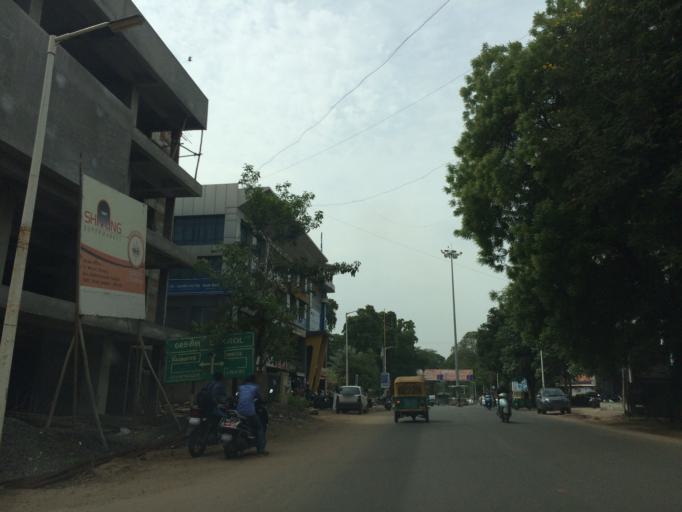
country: IN
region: Gujarat
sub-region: Anand
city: Karamsad
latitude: 22.5491
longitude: 72.9290
